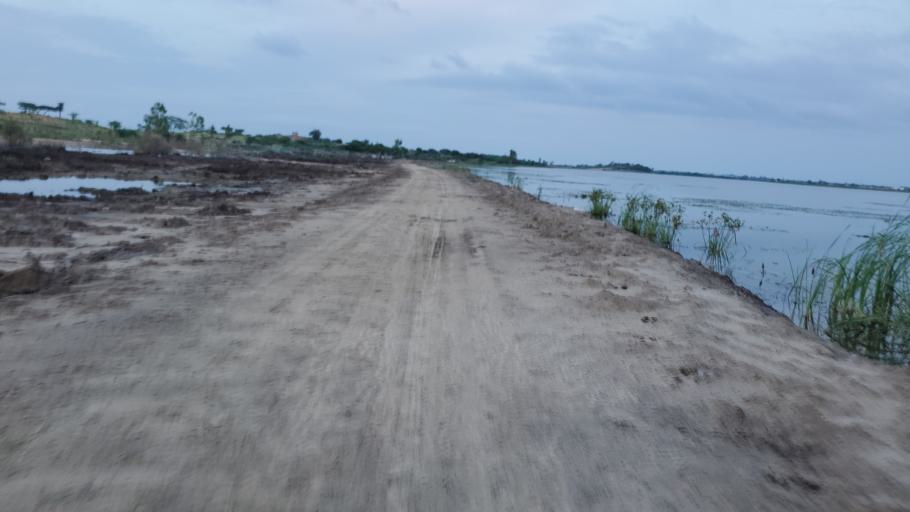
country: SN
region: Saint-Louis
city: Saint-Louis
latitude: 16.0452
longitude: -16.4156
